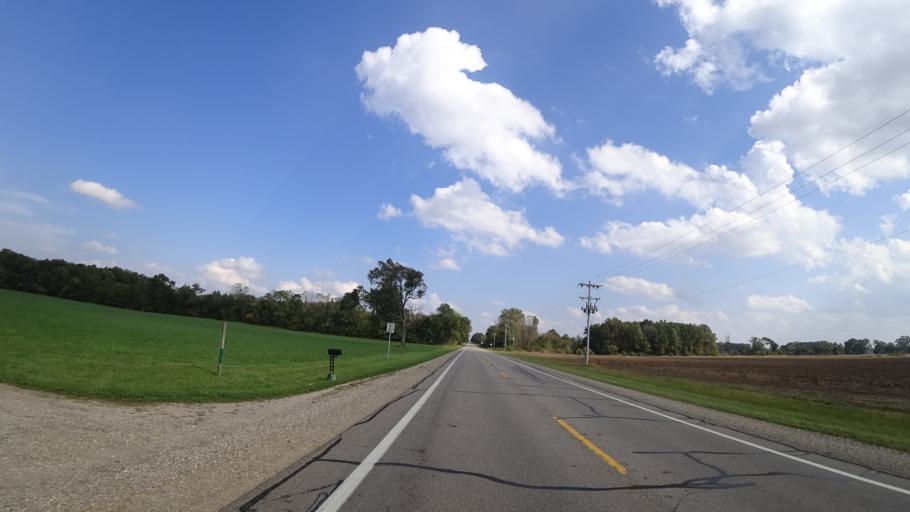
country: US
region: Michigan
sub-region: Saint Joseph County
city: Centreville
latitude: 42.0060
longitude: -85.5420
